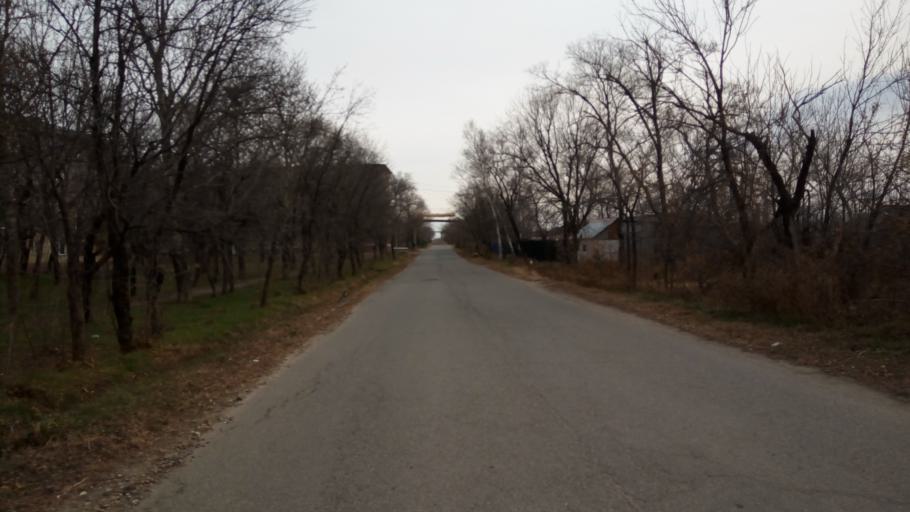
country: RU
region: Primorskiy
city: Novoshakhtinskiy
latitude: 44.0263
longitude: 132.1603
